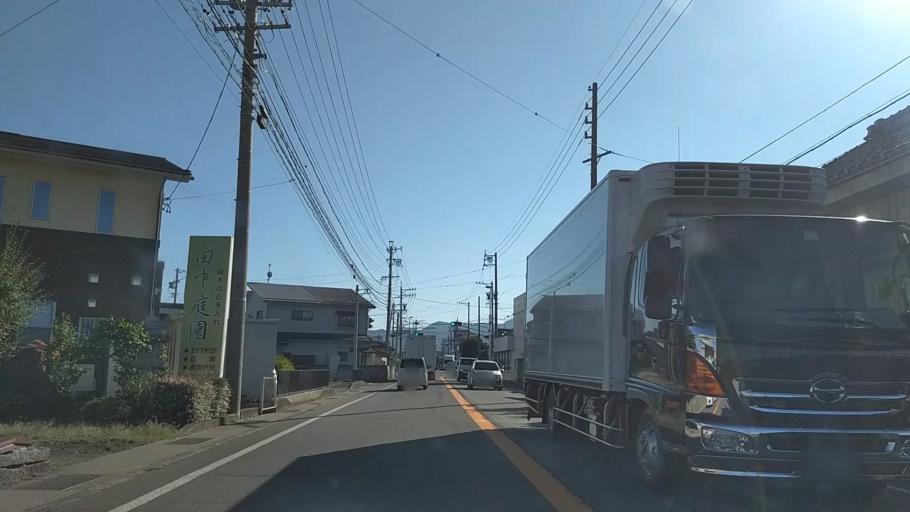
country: JP
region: Nagano
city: Nagano-shi
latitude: 36.5659
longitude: 138.1405
